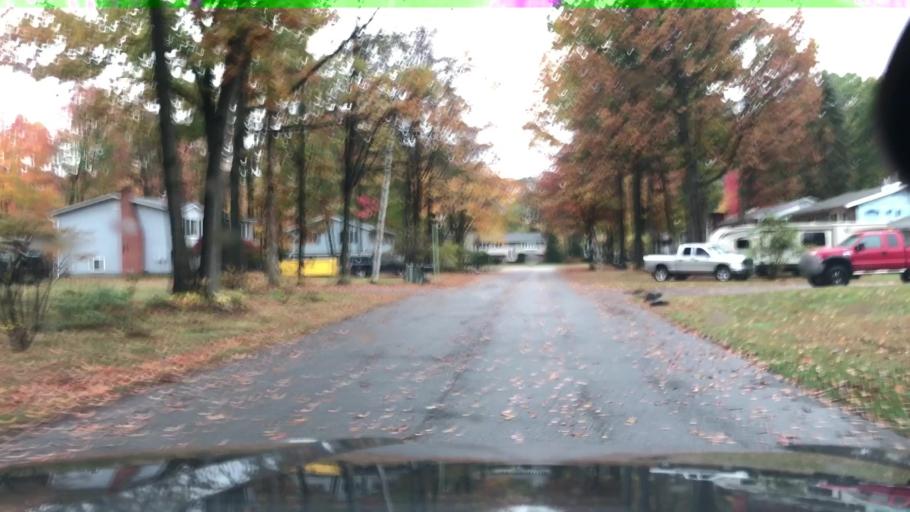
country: US
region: Vermont
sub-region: Chittenden County
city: Burlington
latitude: 44.5424
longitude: -73.2758
